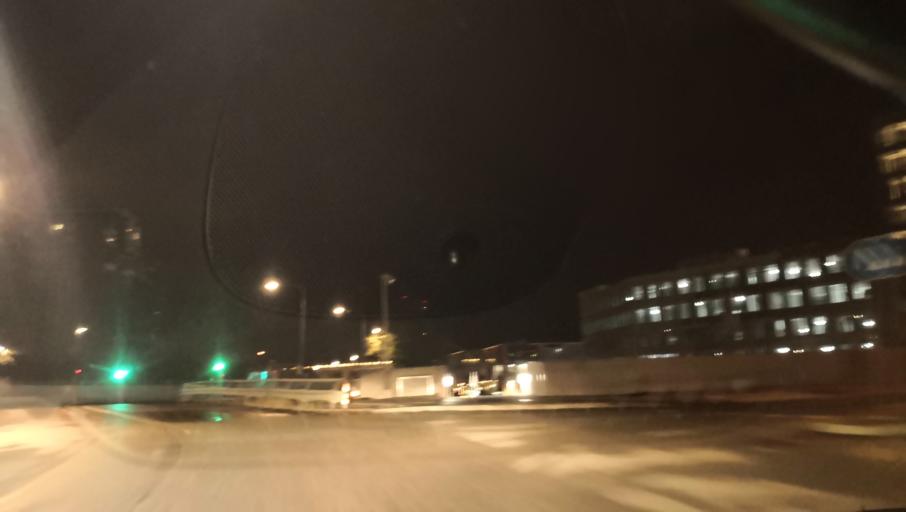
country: SE
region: Stockholm
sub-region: Nacka Kommun
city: Nacka
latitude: 59.3071
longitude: 18.1197
